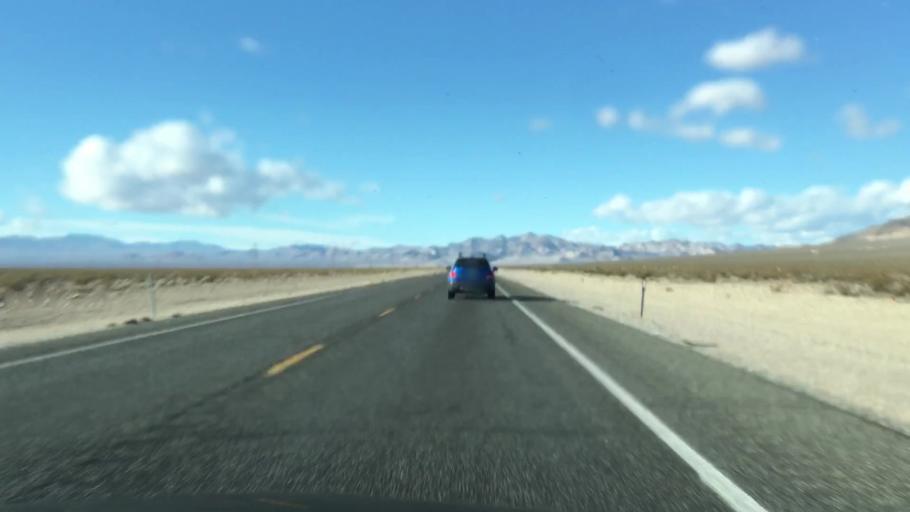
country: US
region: Nevada
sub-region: Nye County
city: Beatty
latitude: 36.7912
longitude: -116.7061
